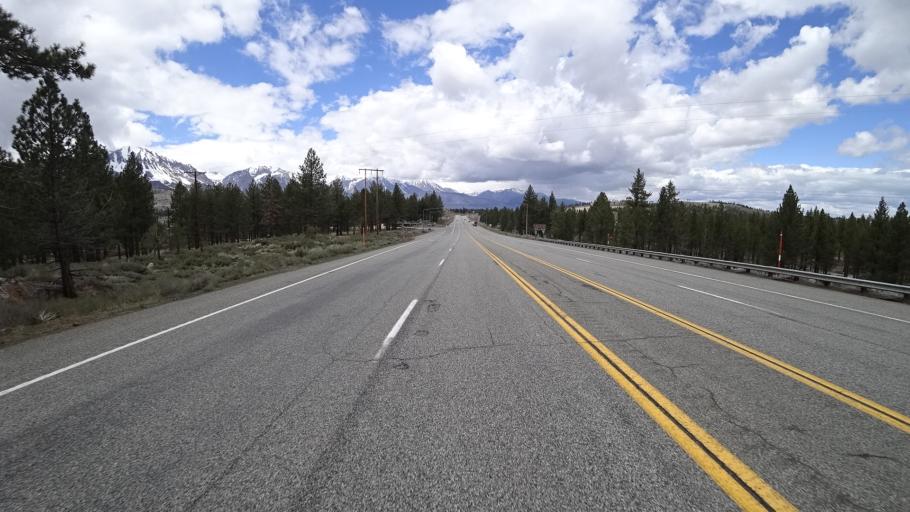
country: US
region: California
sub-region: Mono County
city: Mammoth Lakes
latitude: 37.8111
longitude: -119.0516
